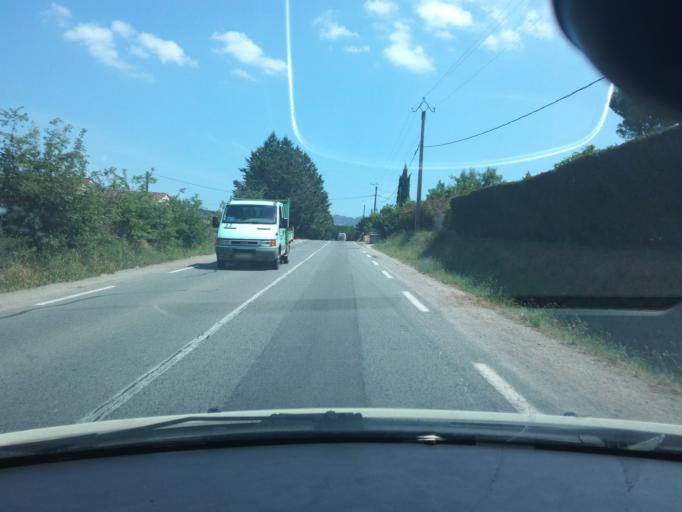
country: FR
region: Provence-Alpes-Cote d'Azur
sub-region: Departement du Var
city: Le Muy
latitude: 43.4881
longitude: 6.5656
